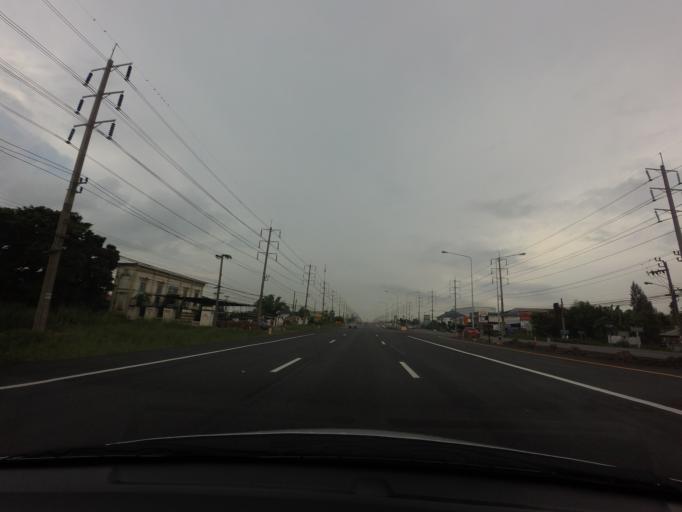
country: TH
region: Bangkok
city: Nong Chok
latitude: 13.8079
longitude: 100.8270
